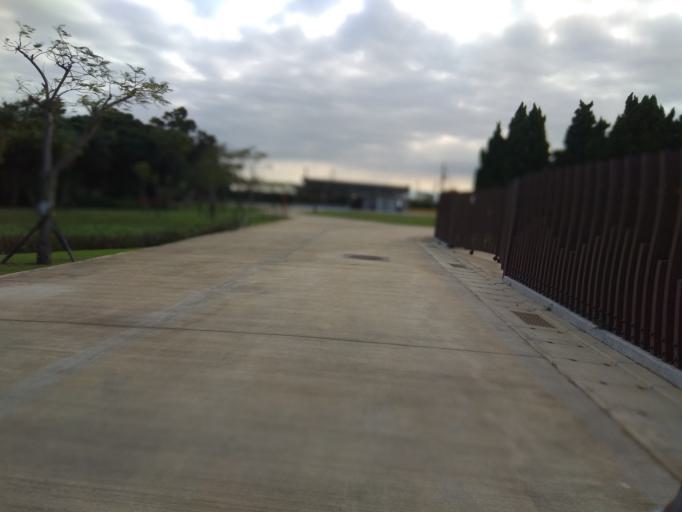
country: TW
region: Taiwan
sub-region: Hsinchu
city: Zhubei
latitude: 25.0074
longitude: 121.0497
